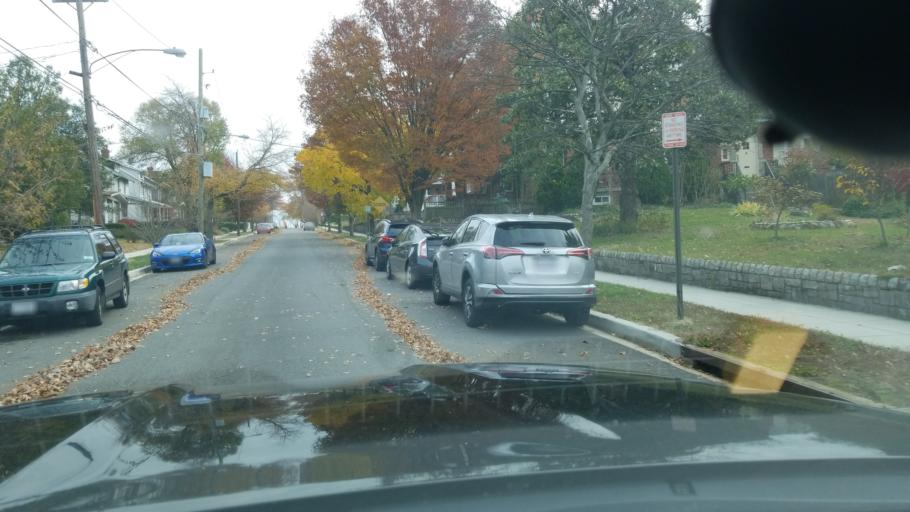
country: US
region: Maryland
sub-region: Montgomery County
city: Takoma Park
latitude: 38.9662
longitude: -77.0159
